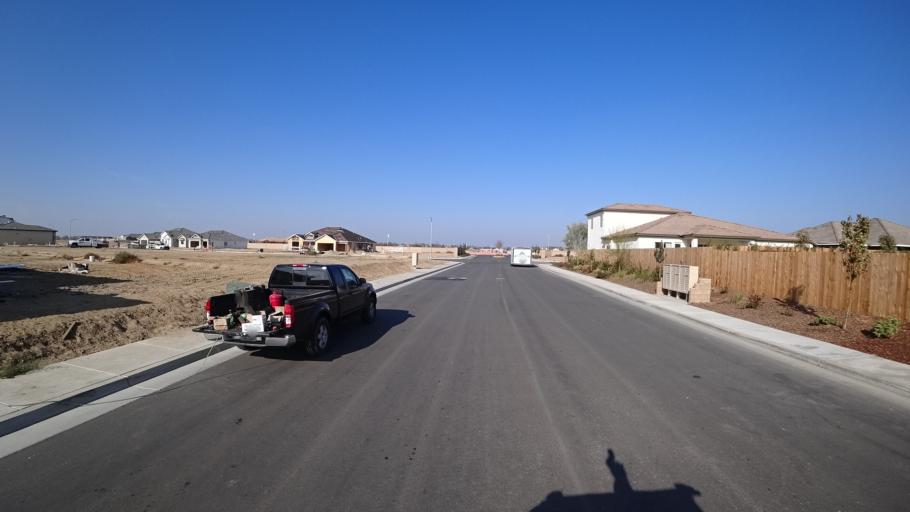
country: US
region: California
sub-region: Kern County
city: Rosedale
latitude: 35.3486
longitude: -119.1766
